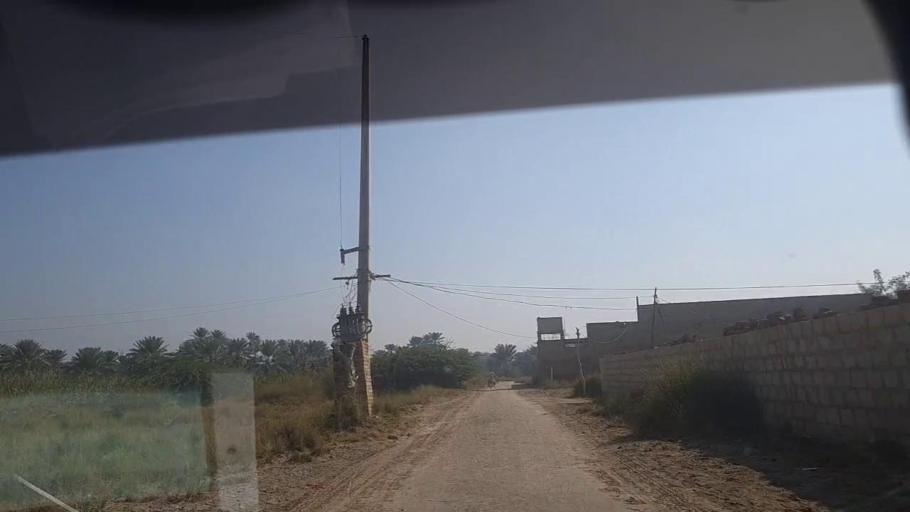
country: PK
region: Sindh
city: Khairpur
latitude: 27.4591
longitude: 68.7403
